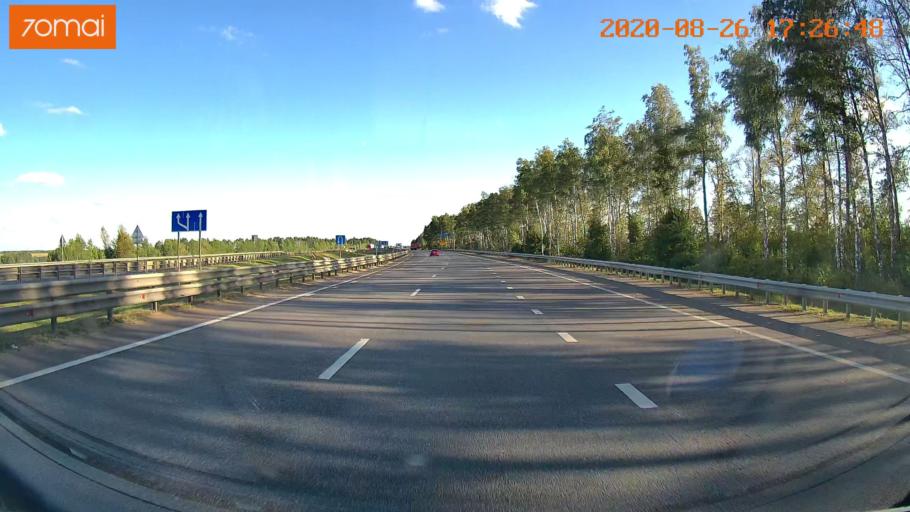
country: RU
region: Tula
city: Kazachka
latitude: 53.4817
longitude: 38.1197
